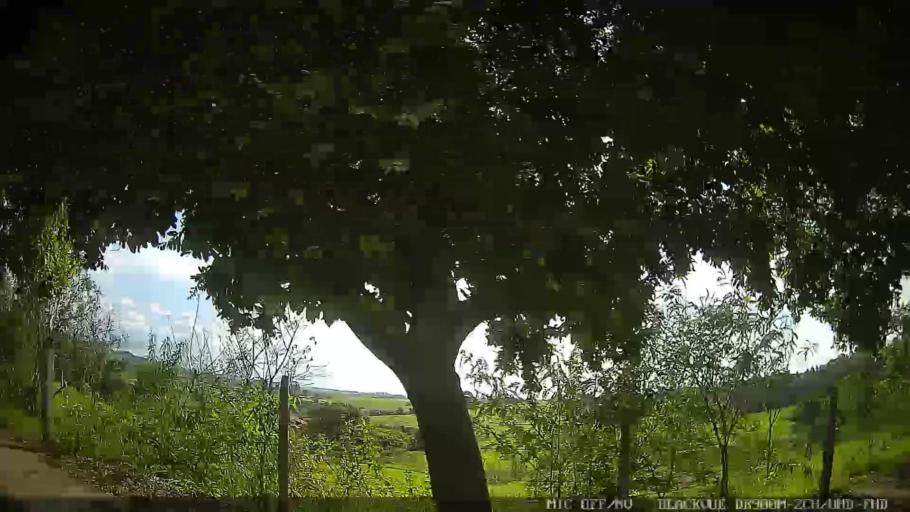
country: BR
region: Sao Paulo
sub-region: Tiete
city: Tiete
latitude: -23.0906
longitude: -47.7800
